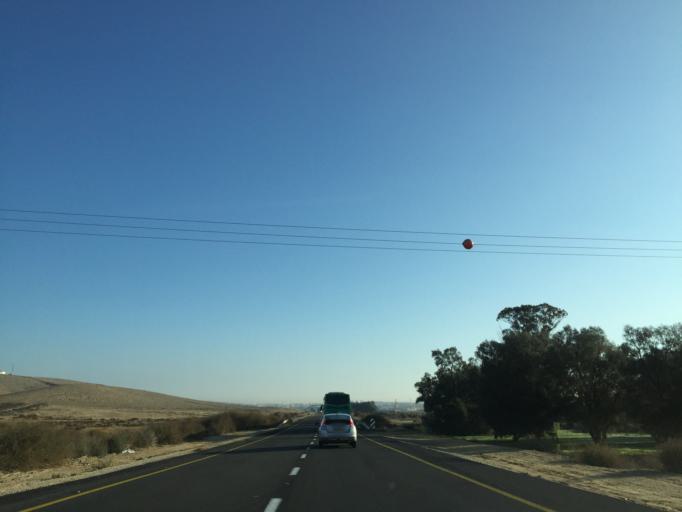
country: IL
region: Southern District
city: Dimona
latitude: 31.0475
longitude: 34.9860
